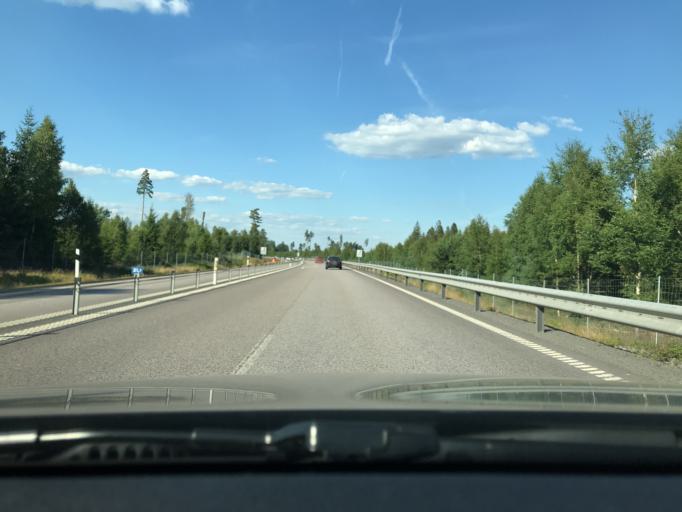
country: SE
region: Kronoberg
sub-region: Alvesta Kommun
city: Vislanda
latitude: 56.6666
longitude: 14.3062
